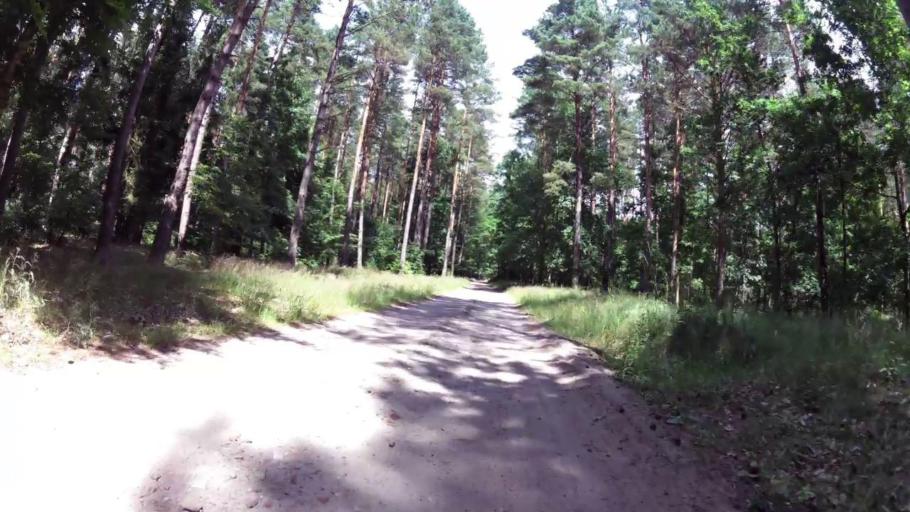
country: PL
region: West Pomeranian Voivodeship
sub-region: Powiat lobeski
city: Lobez
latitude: 53.5741
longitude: 15.6514
